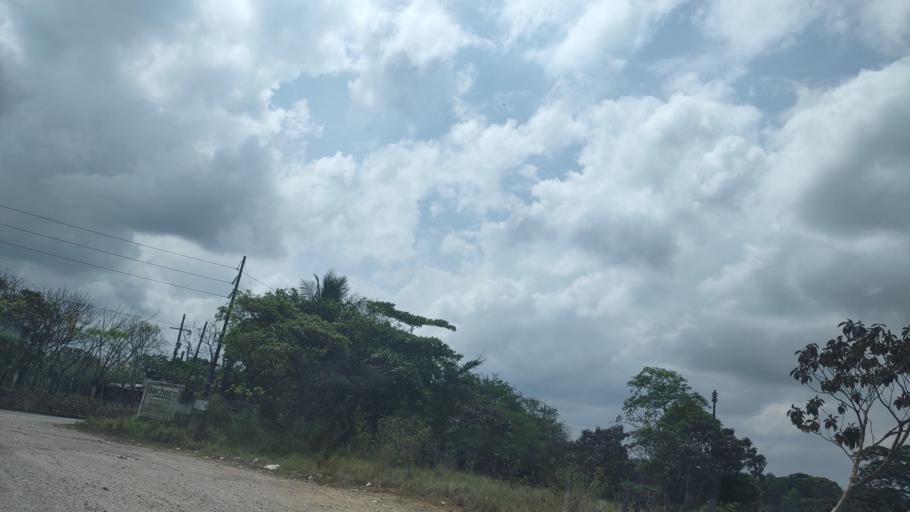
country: MX
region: Veracruz
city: Las Choapas
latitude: 17.9563
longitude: -94.1109
